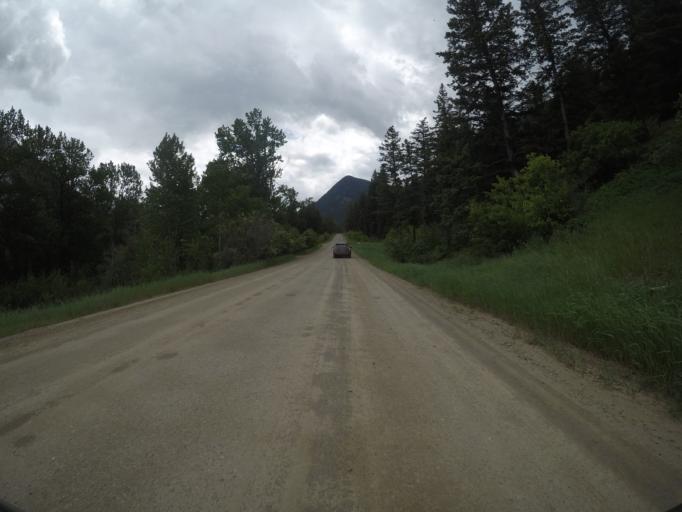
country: US
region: Montana
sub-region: Park County
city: Livingston
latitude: 45.5013
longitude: -110.2272
